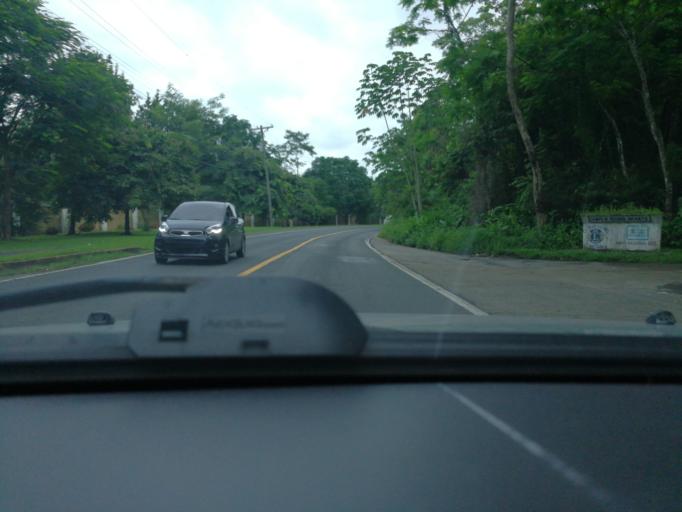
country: PA
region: Panama
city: Panama
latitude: 9.0075
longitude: -79.5451
